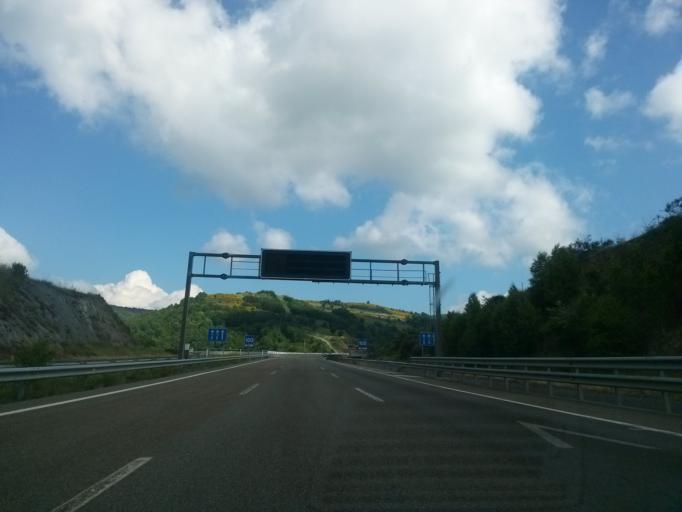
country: ES
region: Galicia
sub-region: Provincia de Lugo
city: San Roman
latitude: 42.7444
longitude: -7.0534
